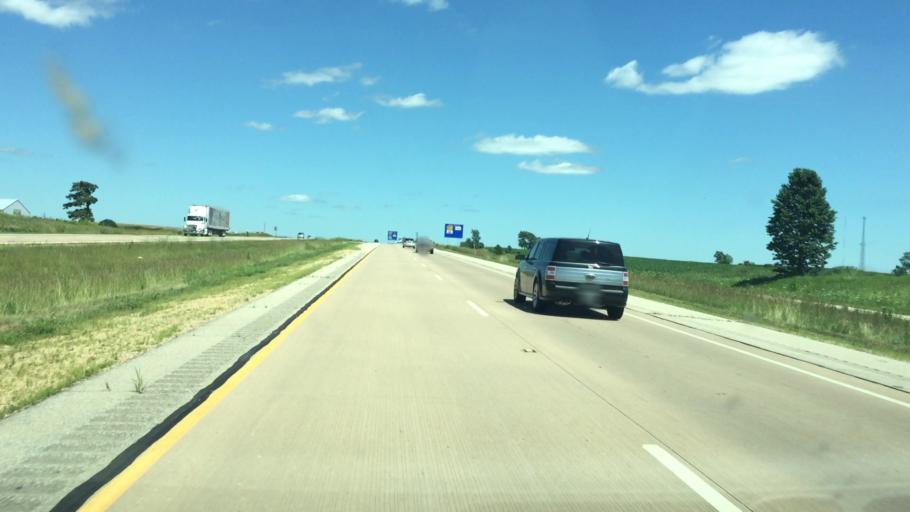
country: US
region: Wisconsin
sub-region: Grant County
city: Platteville
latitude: 42.7109
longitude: -90.5005
